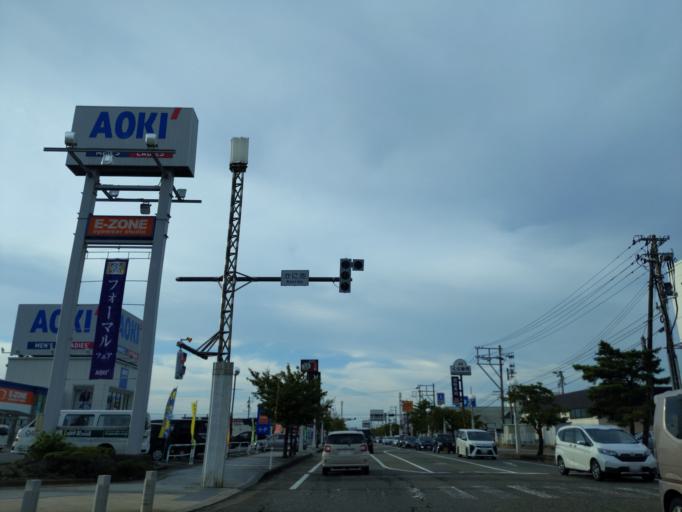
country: JP
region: Niigata
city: Joetsu
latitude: 37.1536
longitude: 138.2553
